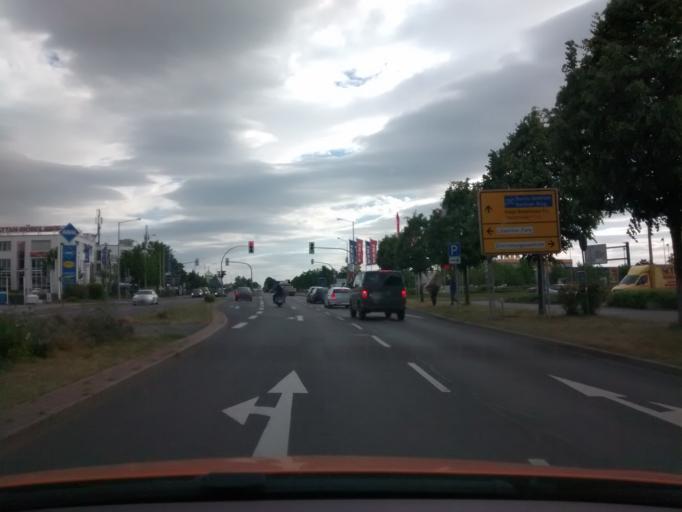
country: DE
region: Brandenburg
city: Schulzendorf
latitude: 52.3684
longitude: 13.5610
